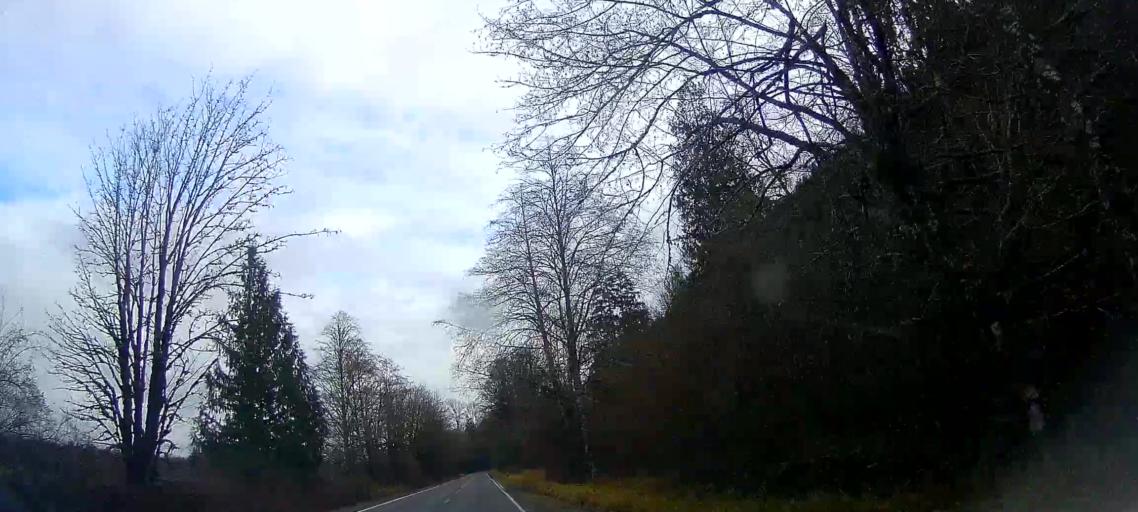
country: US
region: Washington
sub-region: Skagit County
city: Sedro-Woolley
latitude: 48.5147
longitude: -121.9498
